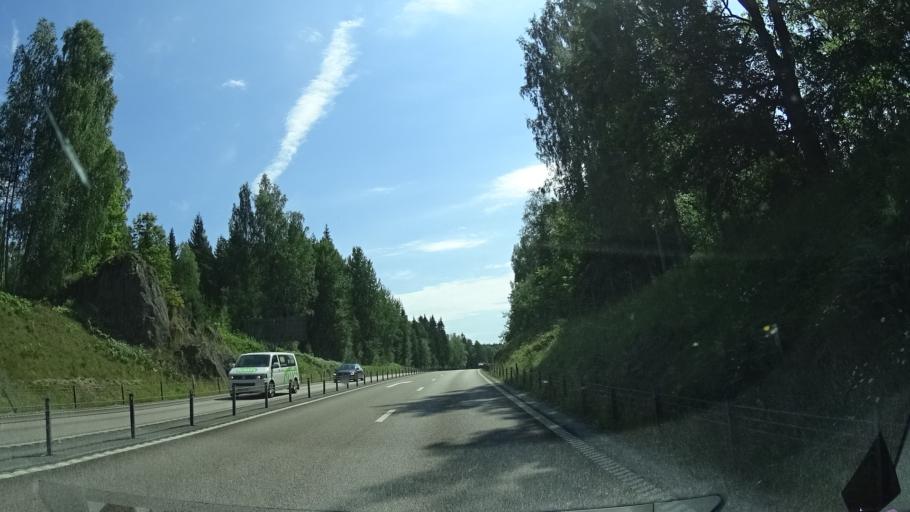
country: SE
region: Vaermland
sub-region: Kristinehamns Kommun
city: Kristinehamn
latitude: 59.3531
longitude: 14.0743
